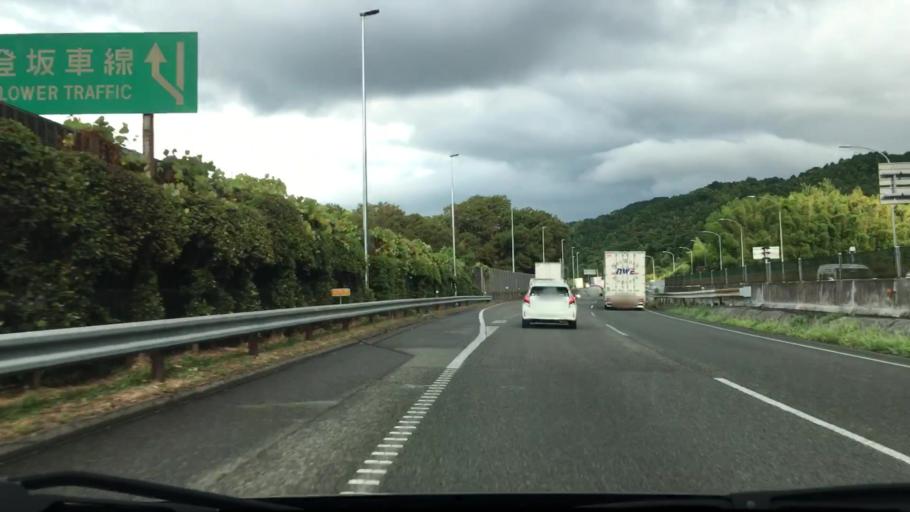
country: JP
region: Fukuoka
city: Nishifukuma
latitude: 33.7507
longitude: 130.5400
